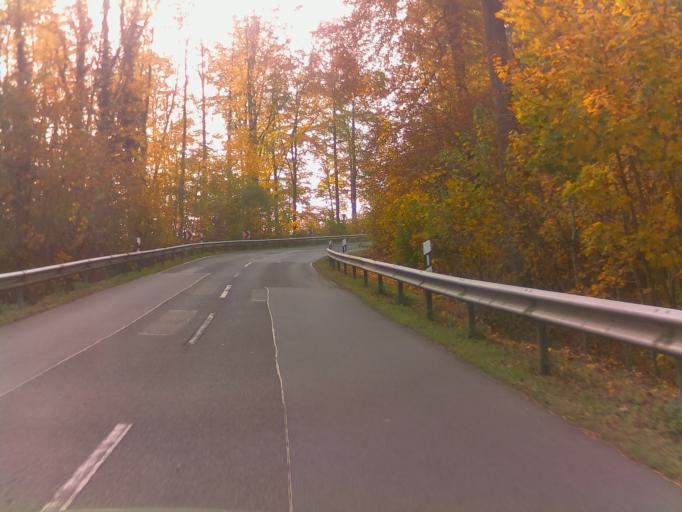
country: DE
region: Baden-Wuerttemberg
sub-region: Karlsruhe Region
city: Reichartshausen
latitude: 49.3649
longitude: 8.9356
